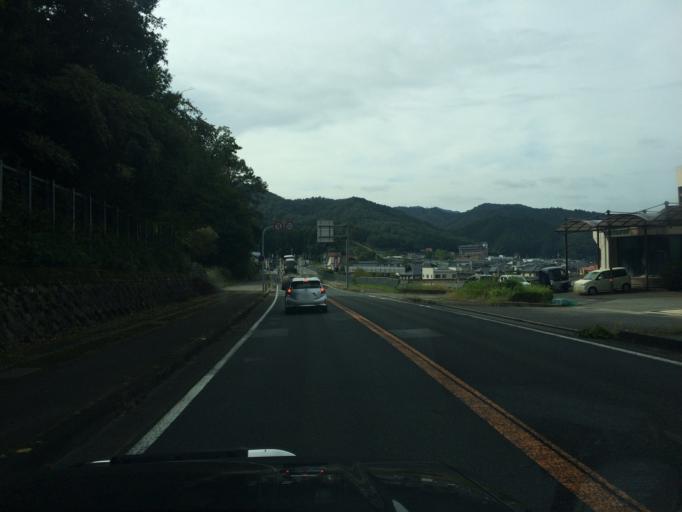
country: JP
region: Hyogo
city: Toyooka
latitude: 35.3388
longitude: 134.8496
